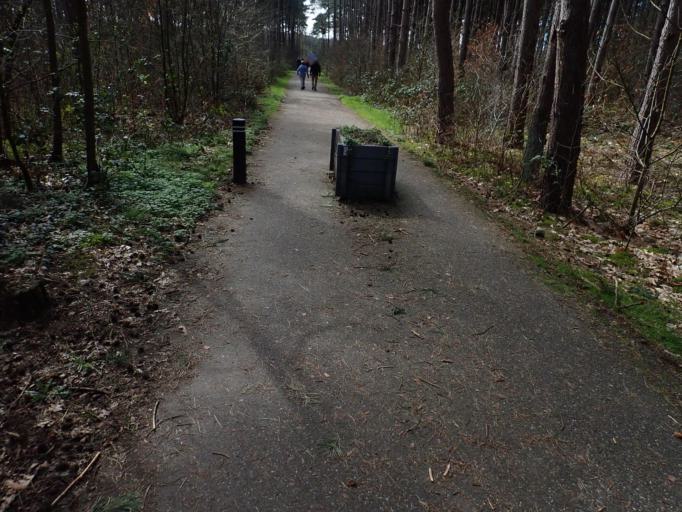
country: BE
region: Flanders
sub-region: Provincie Vlaams-Brabant
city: Scherpenheuvel-Zichem
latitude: 51.0505
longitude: 4.9749
